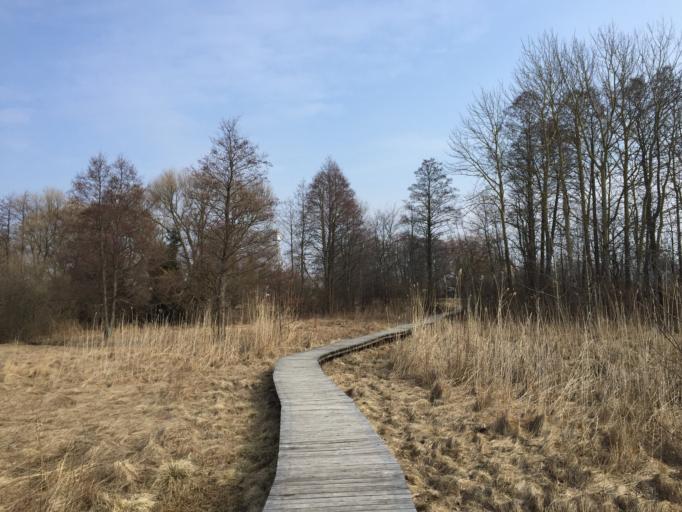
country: LV
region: Salacgrivas
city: Ainazi
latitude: 57.8738
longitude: 24.3590
